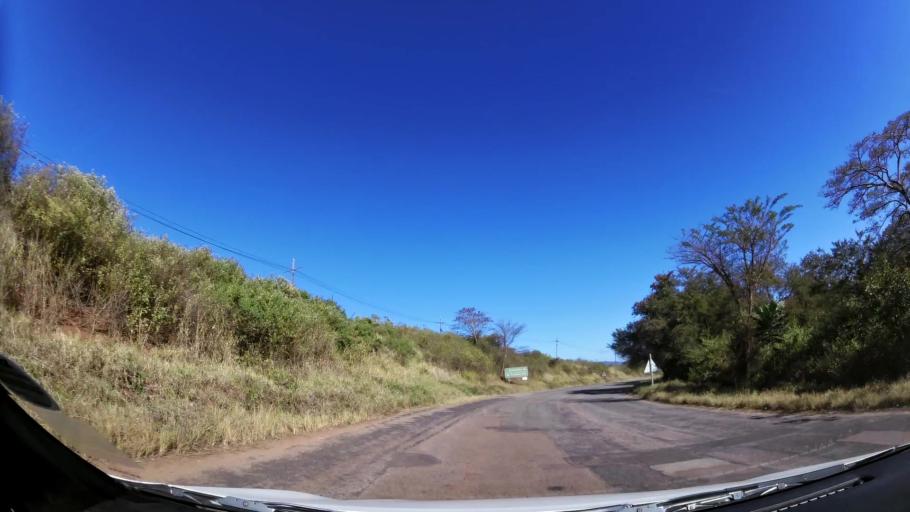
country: ZA
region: Limpopo
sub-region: Mopani District Municipality
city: Tzaneen
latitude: -23.8431
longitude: 30.1932
